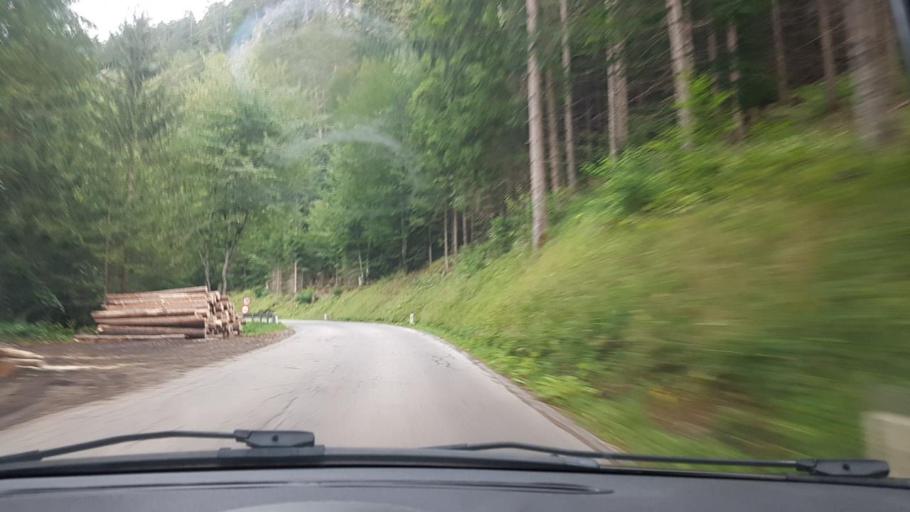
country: AT
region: Tyrol
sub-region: Politischer Bezirk Lienz
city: Tristach
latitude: 46.8117
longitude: 12.7805
